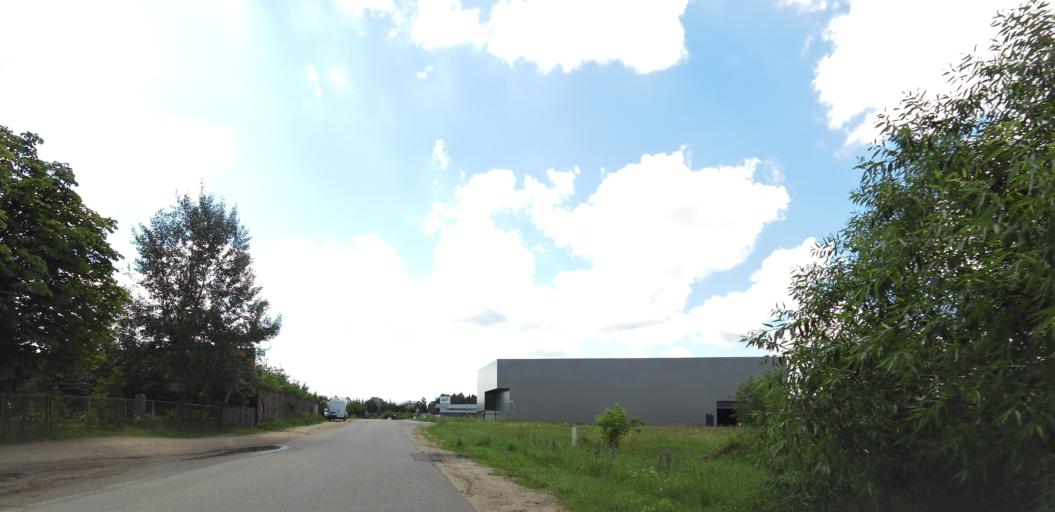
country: LT
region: Vilnius County
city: Pasilaiciai
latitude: 54.7334
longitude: 25.1859
